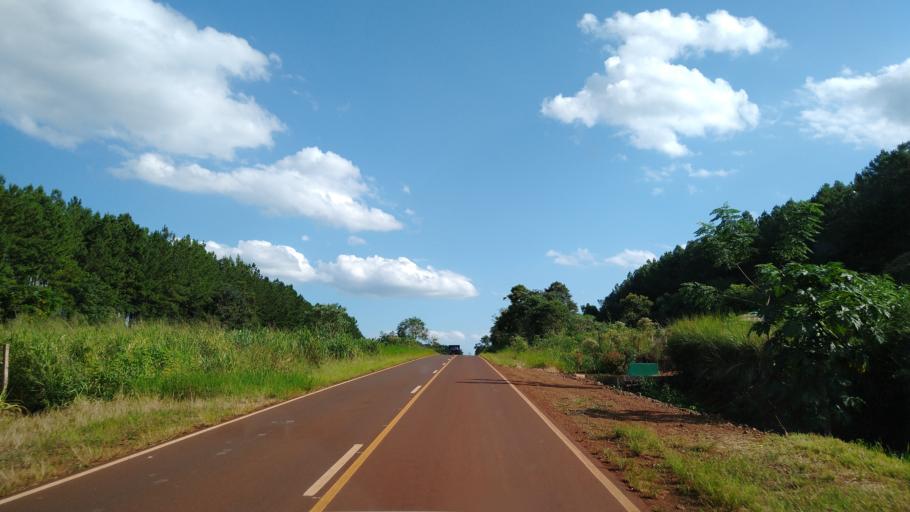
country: AR
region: Misiones
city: Puerto Piray
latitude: -26.4857
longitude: -54.6741
